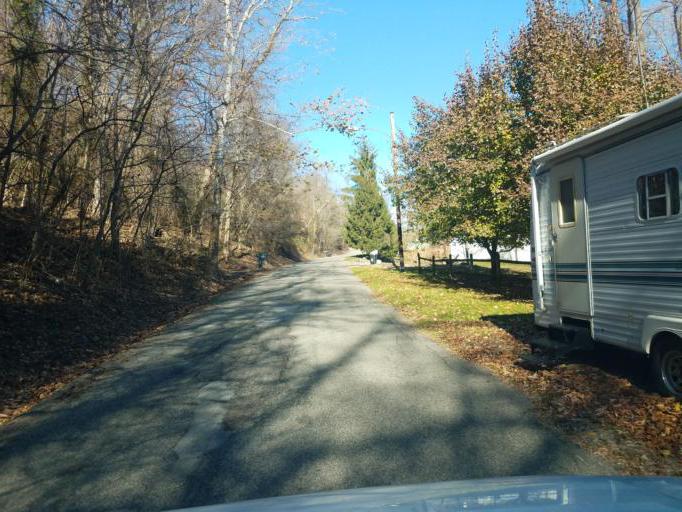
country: US
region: Ohio
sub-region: Scioto County
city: New Boston
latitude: 38.7526
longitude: -82.9636
